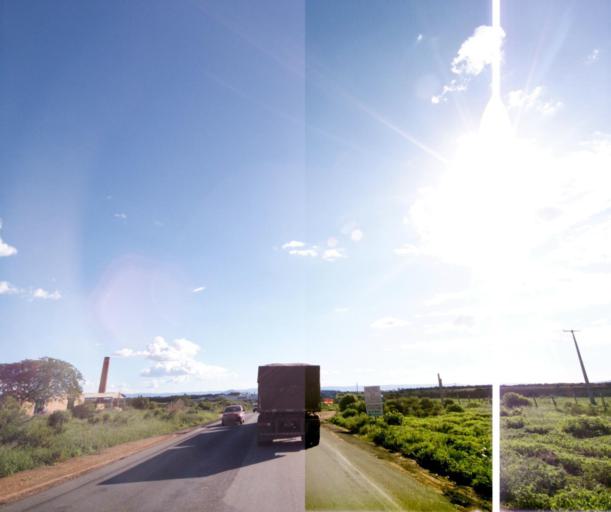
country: BR
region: Bahia
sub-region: Guanambi
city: Guanambi
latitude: -14.1813
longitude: -42.7349
